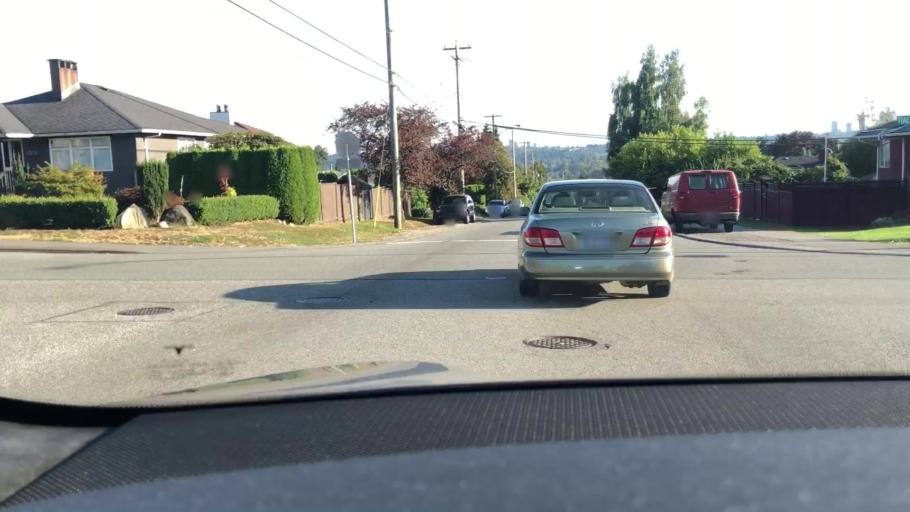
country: CA
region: British Columbia
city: Burnaby
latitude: 49.2681
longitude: -122.9701
